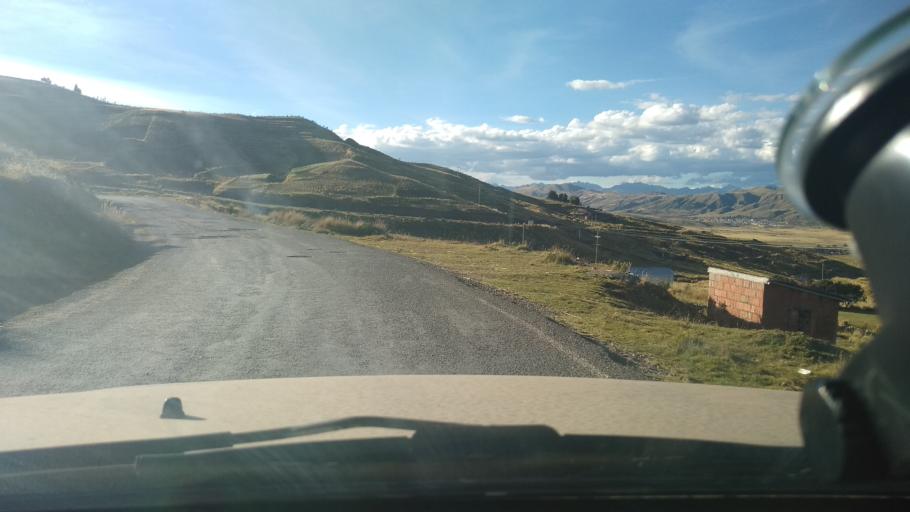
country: PE
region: Cusco
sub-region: Provincia de Canas
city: Ccaquiracunca
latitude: -14.2779
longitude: -71.4486
